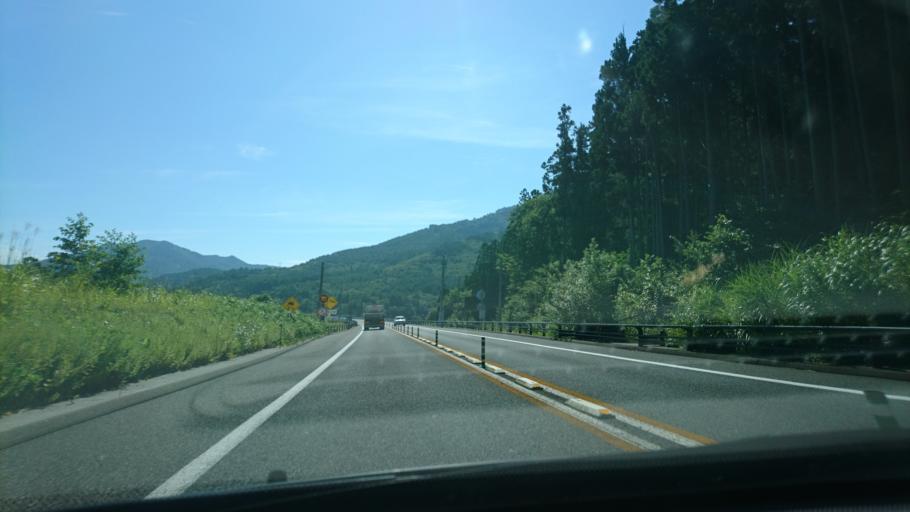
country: JP
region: Iwate
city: Kitakami
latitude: 39.2907
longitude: 141.3205
